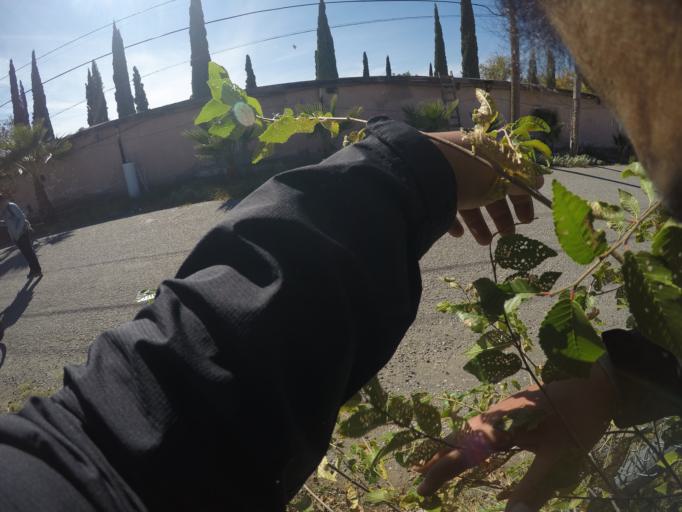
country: MX
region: Chihuahua
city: Ciudad Juarez
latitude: 31.7287
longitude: -106.4223
